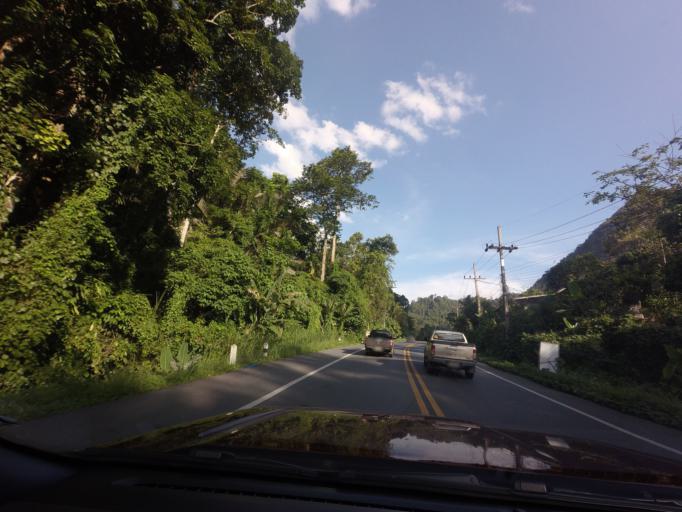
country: TH
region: Yala
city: Than To
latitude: 6.2140
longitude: 101.1663
